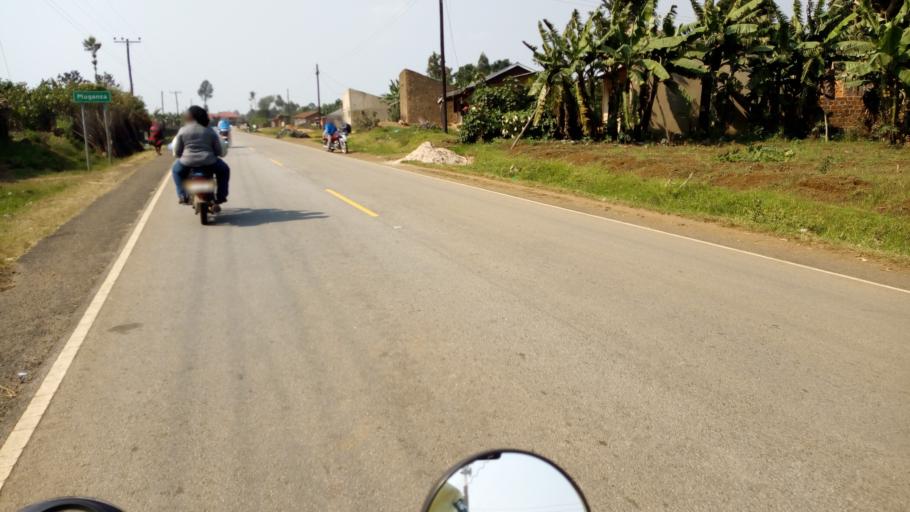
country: UG
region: Western Region
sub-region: Kisoro District
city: Kisoro
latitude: -1.3031
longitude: 29.7238
